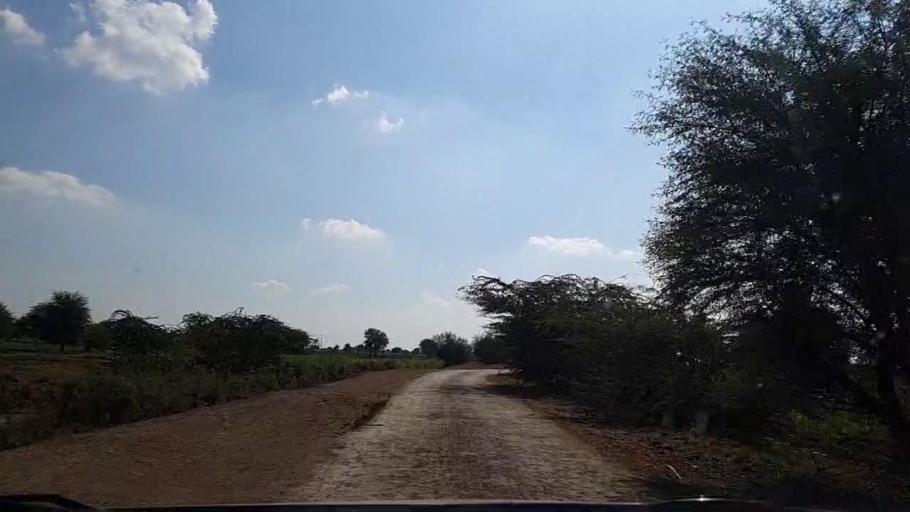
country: PK
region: Sindh
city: Pithoro
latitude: 25.6508
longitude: 69.4486
